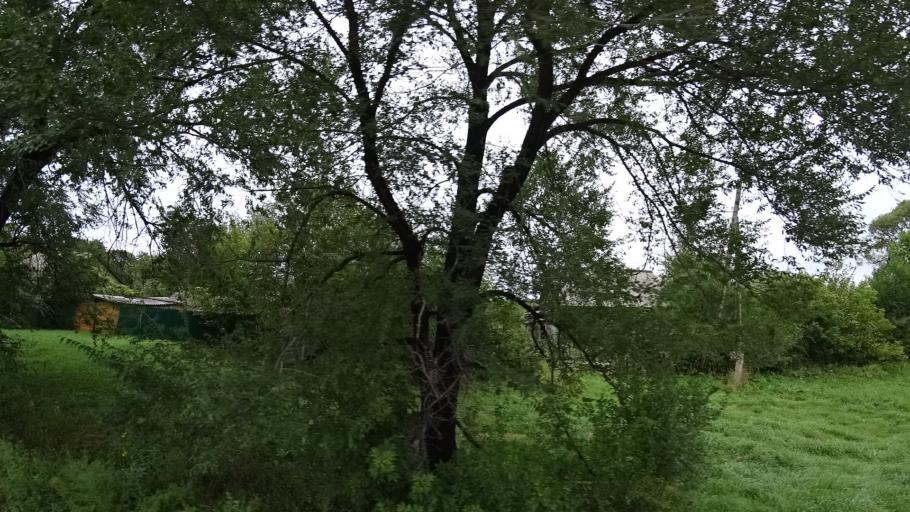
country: RU
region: Primorskiy
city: Monastyrishche
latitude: 44.0881
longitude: 132.5754
